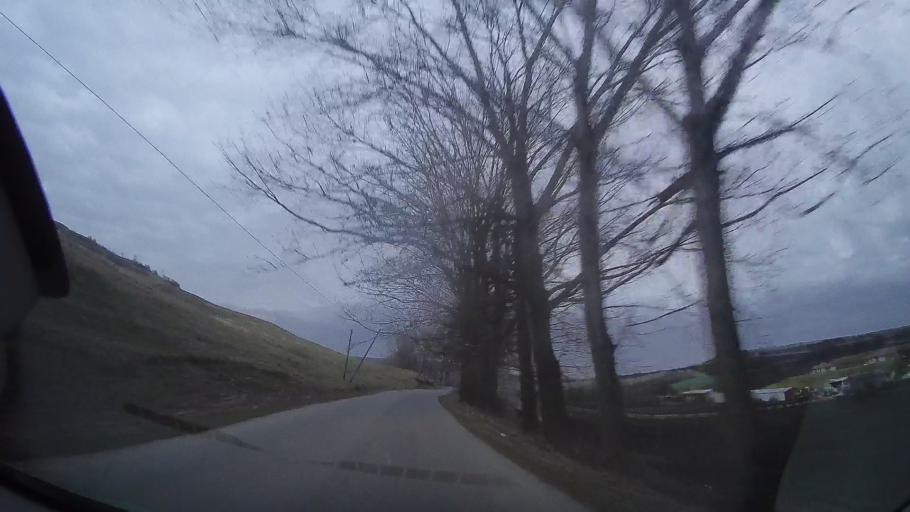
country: RO
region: Cluj
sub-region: Comuna Caianu
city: Vaida-Camaras
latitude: 46.8124
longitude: 23.9294
